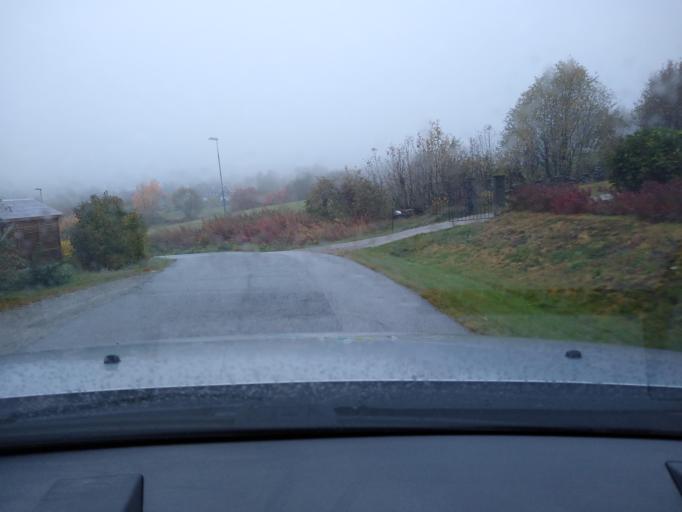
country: NO
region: Oppland
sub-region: Ringebu
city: Ringebu
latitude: 61.5322
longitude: 10.1506
